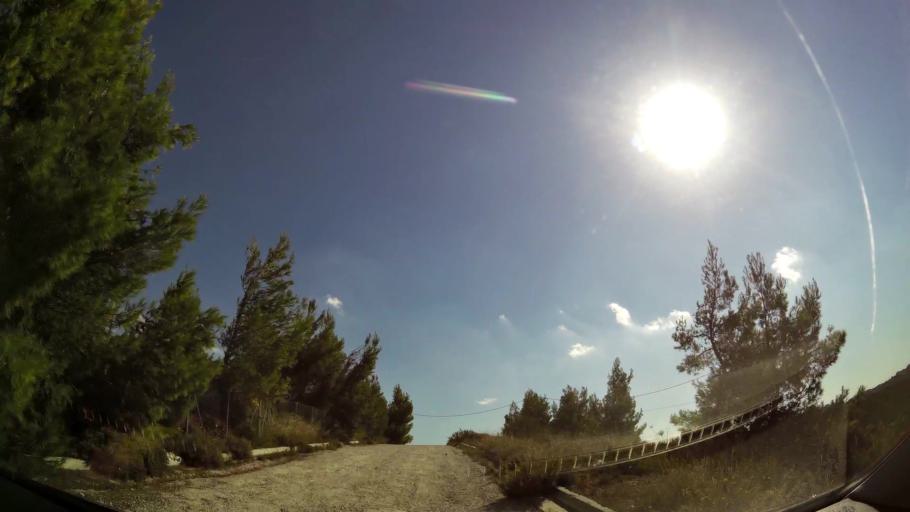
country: GR
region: Attica
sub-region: Nomarchia Anatolikis Attikis
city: Dioni
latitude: 38.0309
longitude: 23.9220
